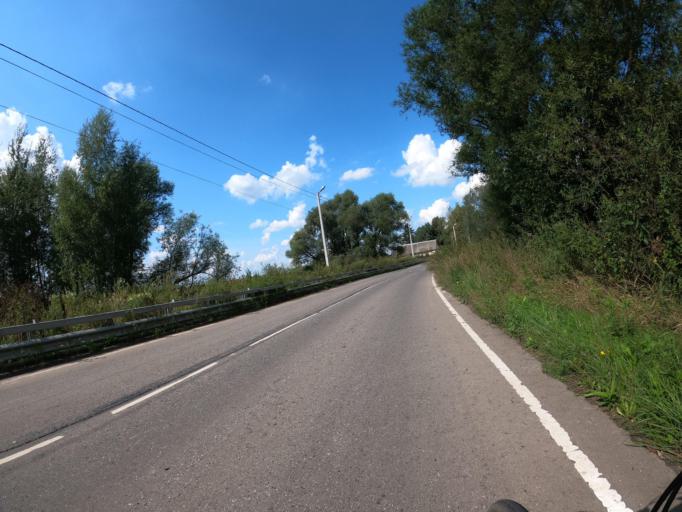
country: RU
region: Moskovskaya
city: Troitskoye
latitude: 55.2463
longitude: 38.5770
